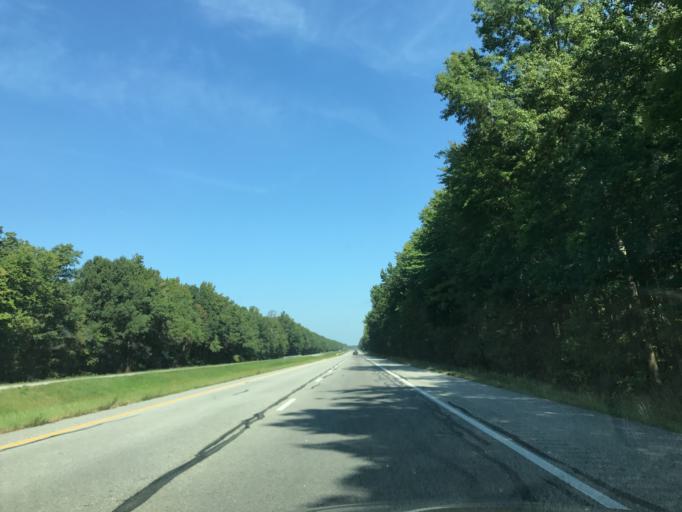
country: US
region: Delaware
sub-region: New Castle County
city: Townsend
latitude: 39.2972
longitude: -75.8524
